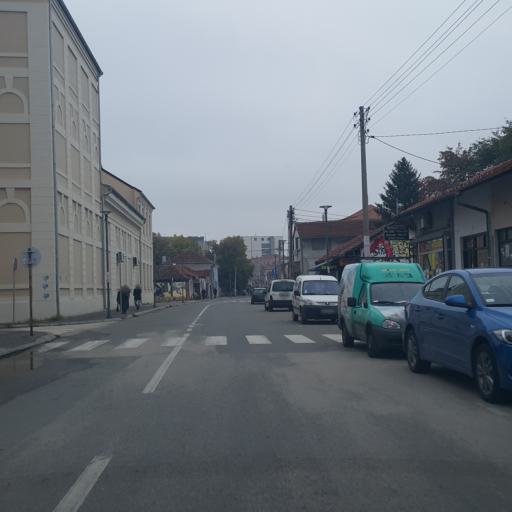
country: RS
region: Central Serbia
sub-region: Zajecarski Okrug
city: Zajecar
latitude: 43.9007
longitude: 22.2742
